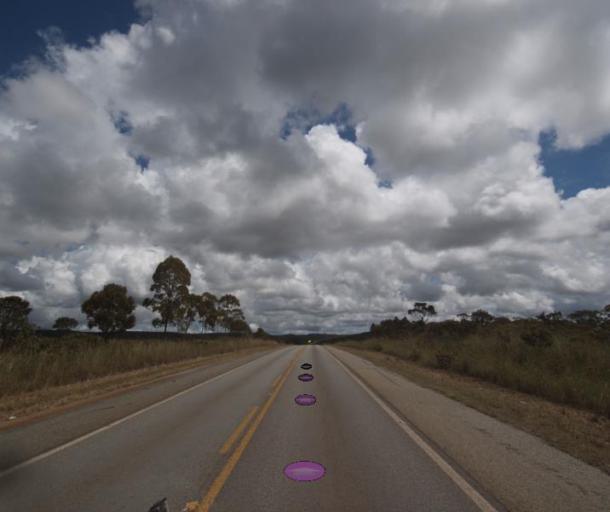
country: BR
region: Goias
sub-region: Pirenopolis
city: Pirenopolis
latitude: -15.7655
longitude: -48.7080
